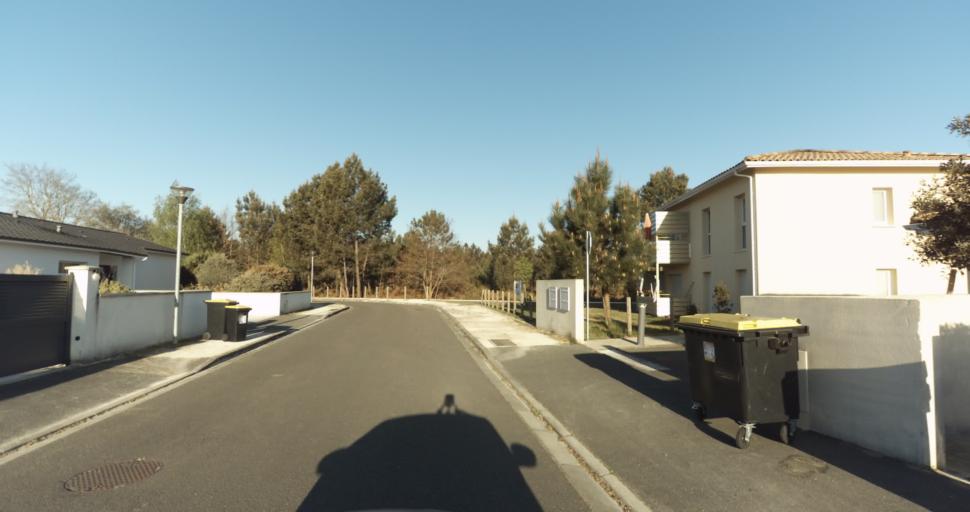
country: FR
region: Aquitaine
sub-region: Departement de la Gironde
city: Martignas-sur-Jalle
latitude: 44.8166
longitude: -0.7823
